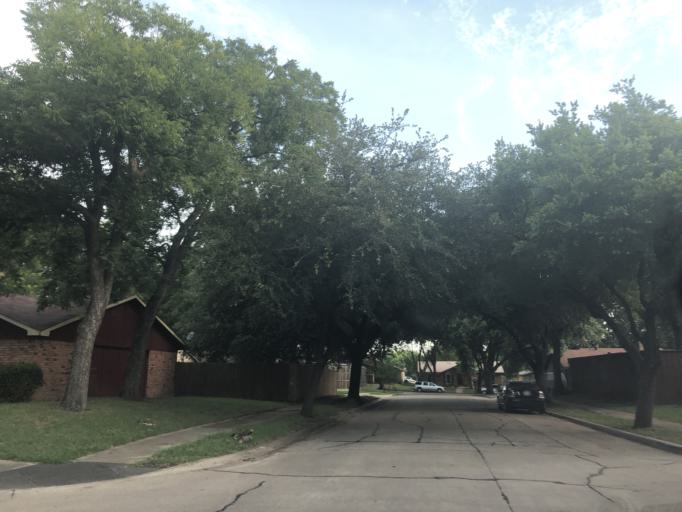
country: US
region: Texas
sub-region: Dallas County
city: Sunnyvale
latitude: 32.8401
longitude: -96.5869
